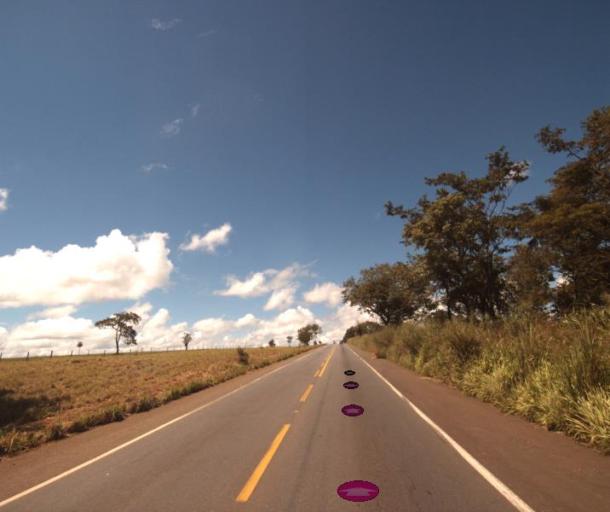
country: BR
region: Goias
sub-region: Jaragua
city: Jaragua
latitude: -15.8240
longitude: -49.2839
